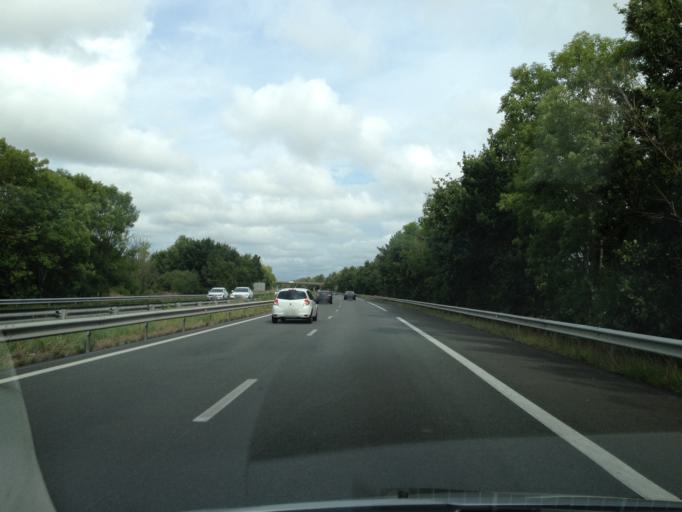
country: FR
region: Aquitaine
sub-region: Departement du Lot-et-Garonne
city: Roquefort
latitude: 44.1769
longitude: 0.5723
